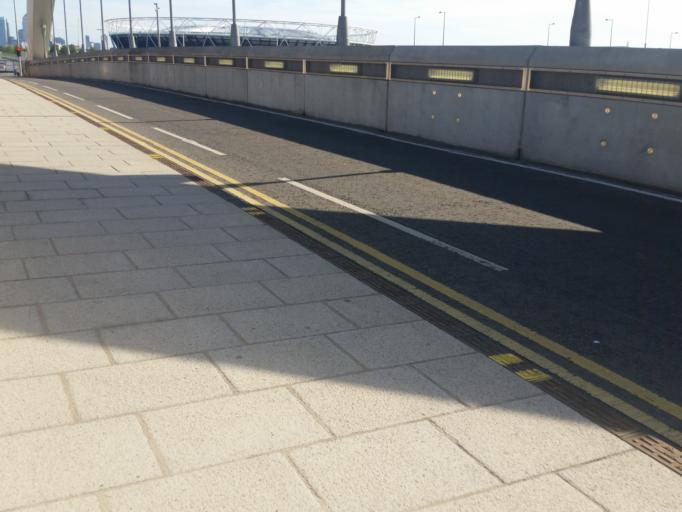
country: GB
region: England
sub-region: Greater London
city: Poplar
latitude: 51.5452
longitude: -0.0125
